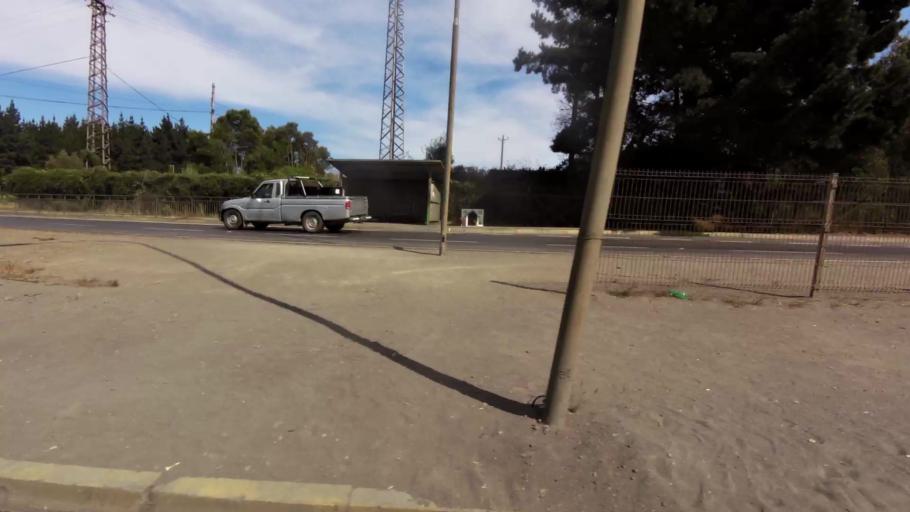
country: CL
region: Biobio
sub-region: Provincia de Concepcion
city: Talcahuano
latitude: -36.7519
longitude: -73.1238
